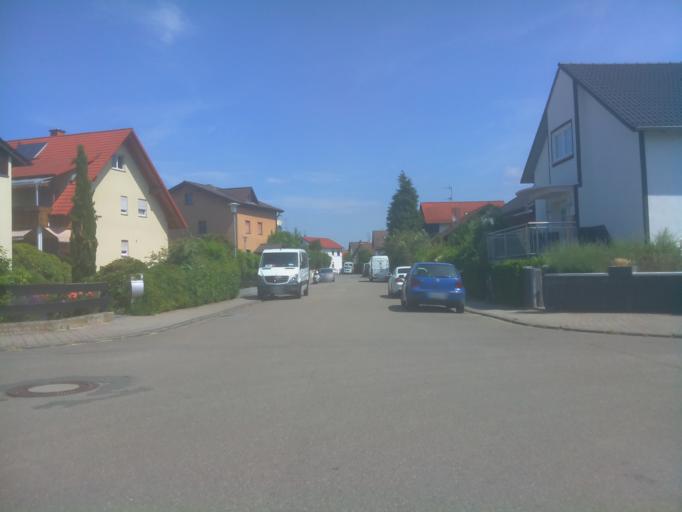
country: DE
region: Baden-Wuerttemberg
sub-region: Karlsruhe Region
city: Hemsbach
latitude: 49.5877
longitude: 8.6438
